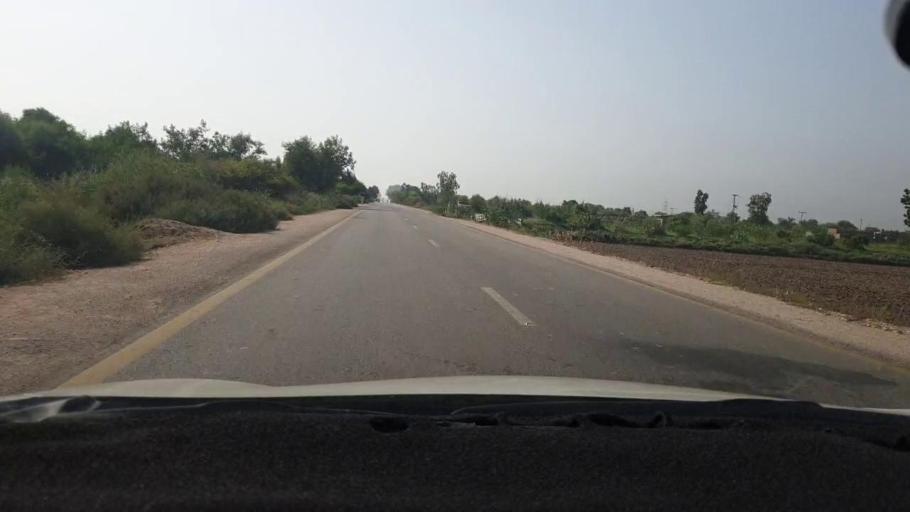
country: PK
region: Sindh
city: Sanghar
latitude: 25.9999
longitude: 68.9625
